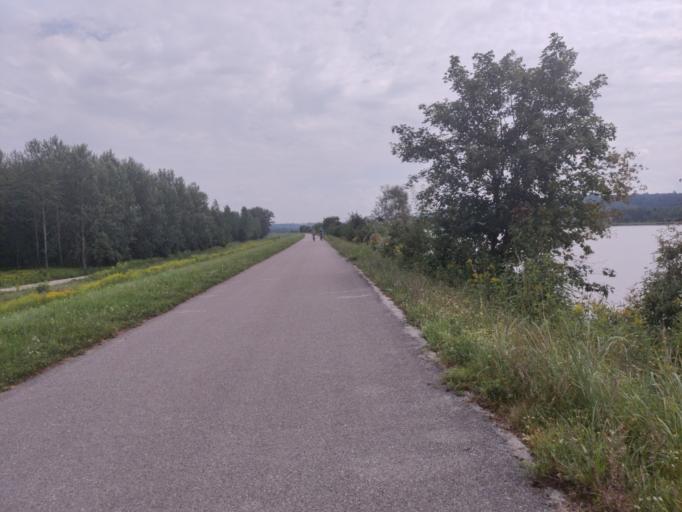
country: AT
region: Lower Austria
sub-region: Politischer Bezirk Amstetten
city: Strengberg
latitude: 48.1732
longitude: 14.6506
